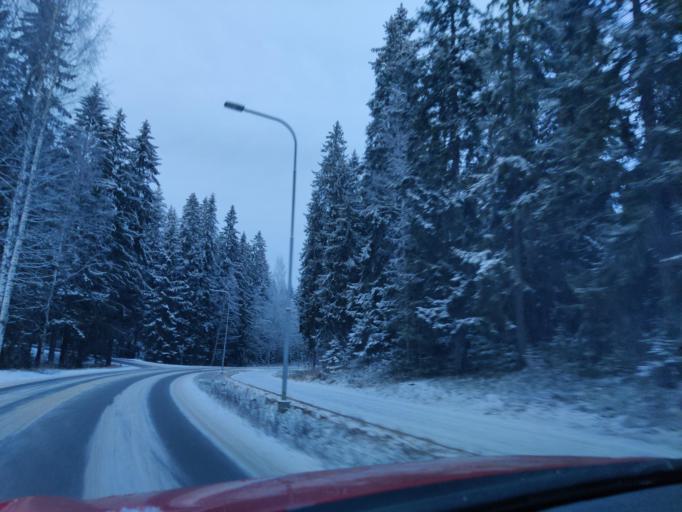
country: FI
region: Pirkanmaa
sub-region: Tampere
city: Tampere
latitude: 61.5099
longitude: 23.7942
